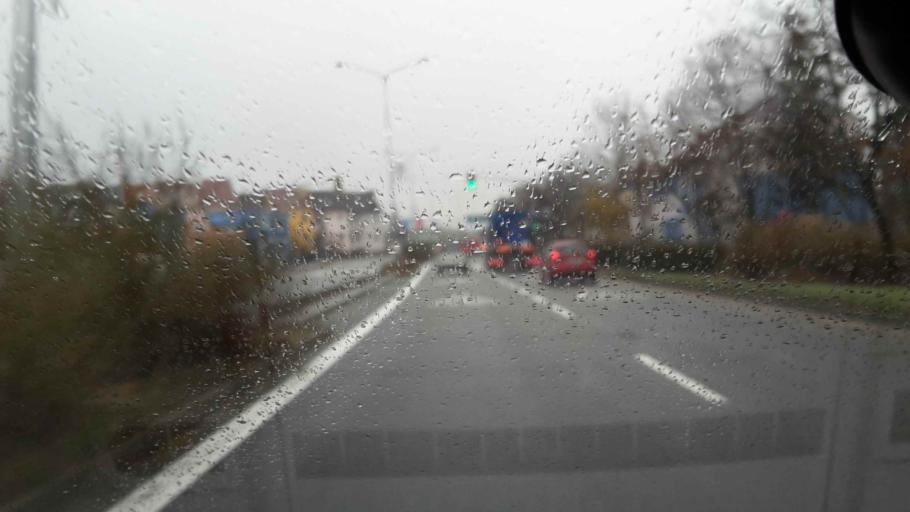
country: CZ
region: South Moravian
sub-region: Mesto Brno
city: Brno
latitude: 49.1929
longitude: 16.6473
